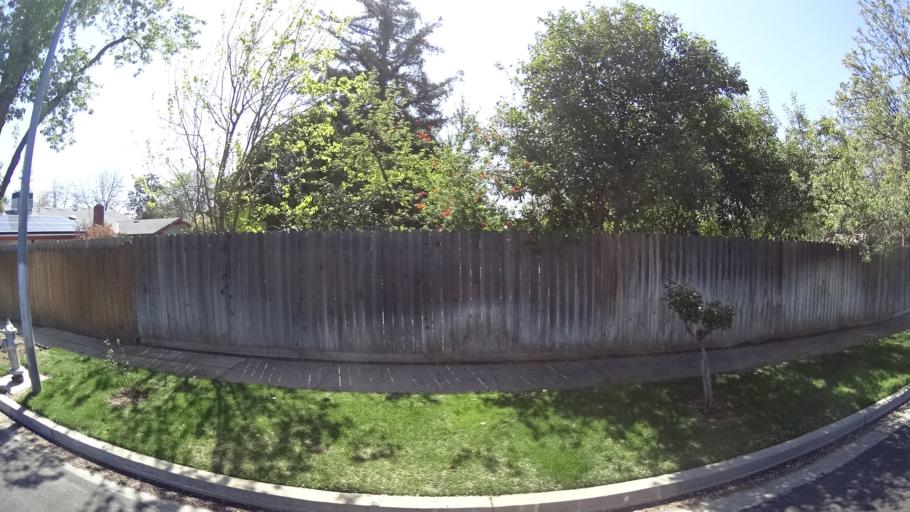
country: US
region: California
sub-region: Fresno County
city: Fresno
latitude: 36.8111
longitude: -119.7979
